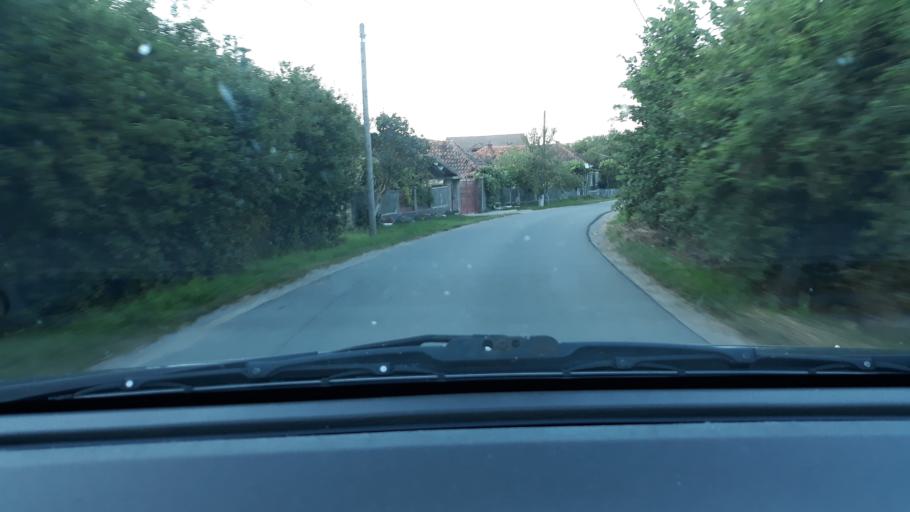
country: RO
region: Bihor
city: Hidiselu de Sus
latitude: 46.9426
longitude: 22.0201
